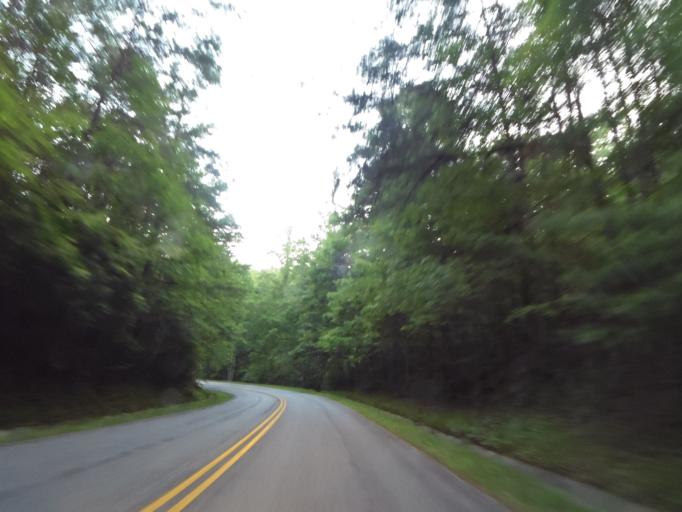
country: US
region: Tennessee
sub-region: Blount County
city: Maryville
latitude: 35.5885
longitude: -83.9964
